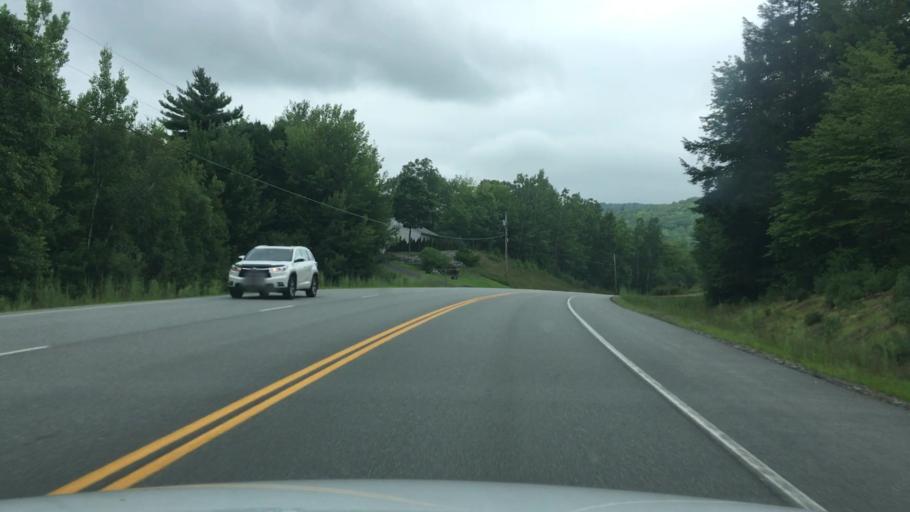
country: US
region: Maine
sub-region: Penobscot County
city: Bradley
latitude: 44.8243
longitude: -68.4925
